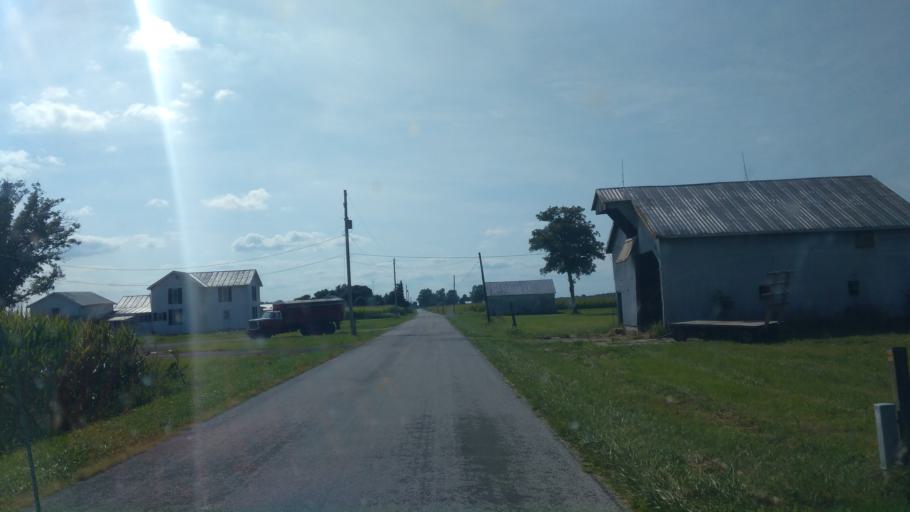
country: US
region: Ohio
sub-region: Hardin County
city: Forest
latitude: 40.6876
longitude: -83.4585
